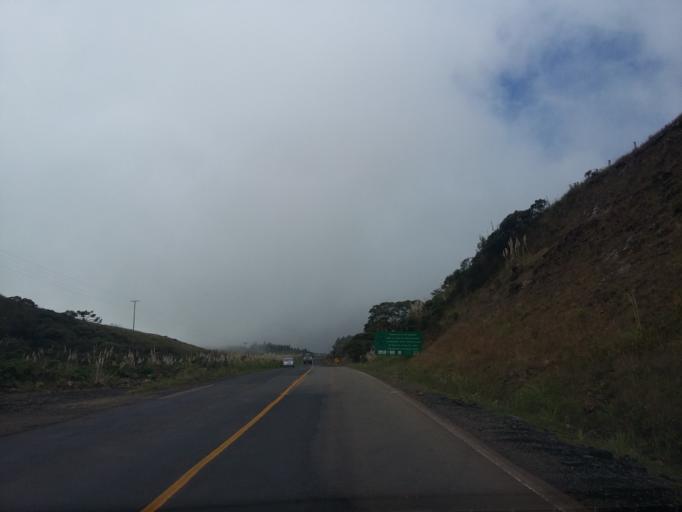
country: BR
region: Santa Catarina
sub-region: Lauro Muller
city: Lauro Muller
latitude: -28.3801
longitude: -49.5575
